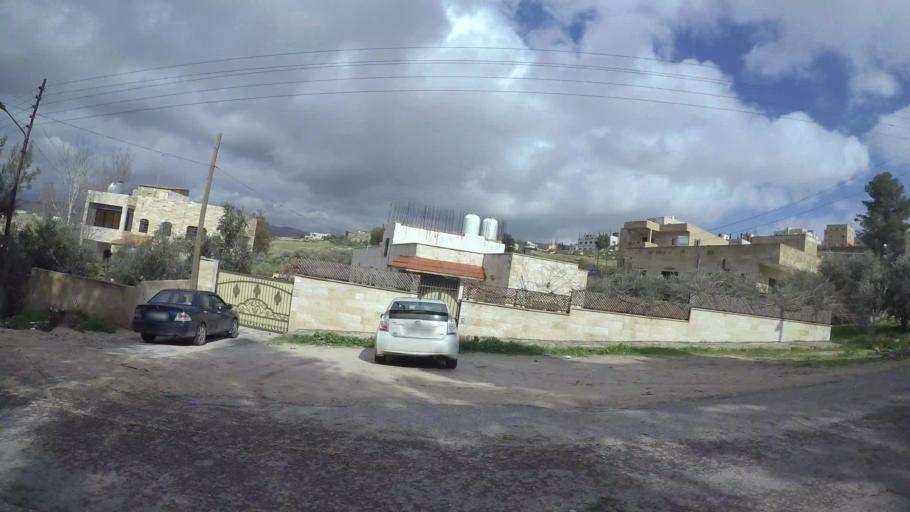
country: JO
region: Amman
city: Al Jubayhah
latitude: 32.0741
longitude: 35.8629
